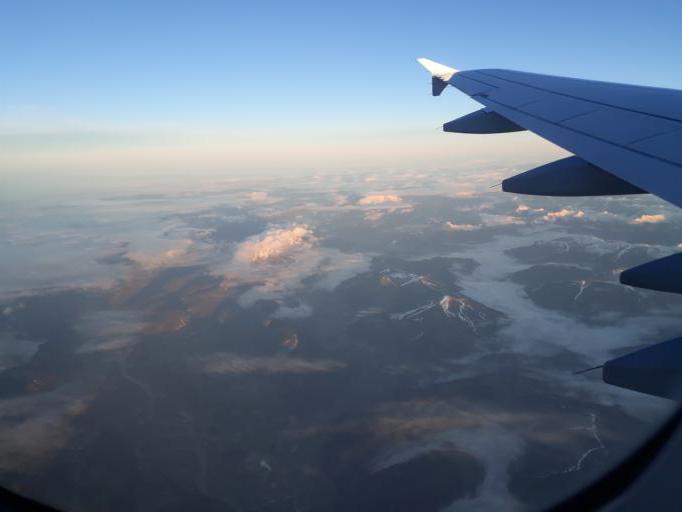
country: AT
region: Tyrol
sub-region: Politischer Bezirk Kufstein
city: Radfeld
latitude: 47.4513
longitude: 11.9398
